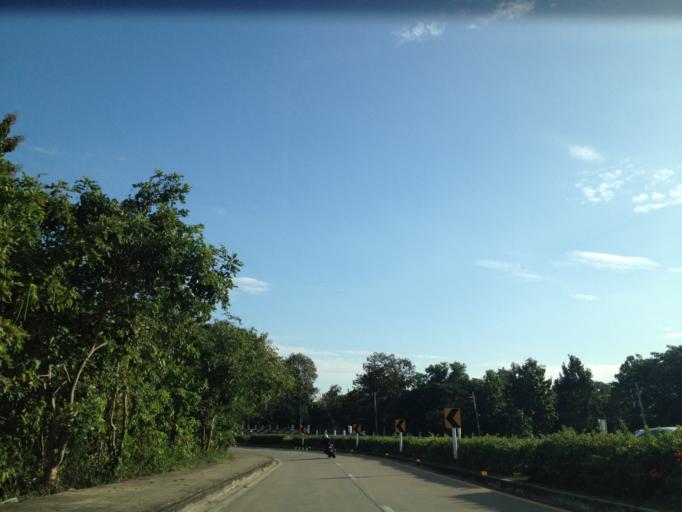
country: TH
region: Chiang Mai
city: Chiang Mai
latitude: 18.8459
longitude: 98.9599
